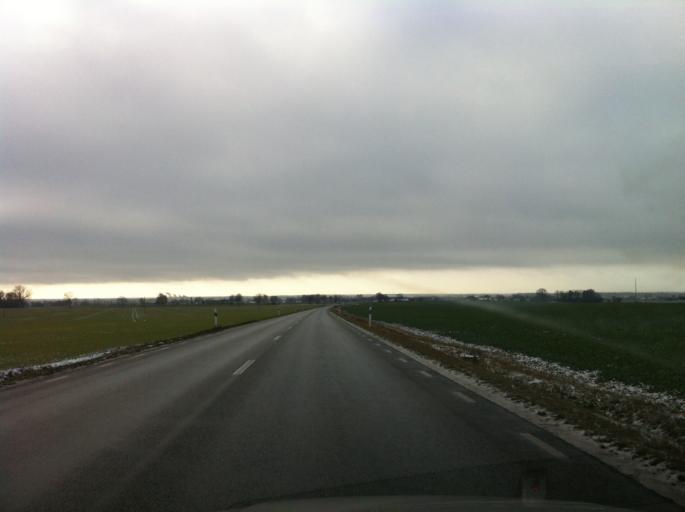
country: SE
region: Skane
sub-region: Svalovs Kommun
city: Teckomatorp
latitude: 55.8947
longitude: 13.0242
